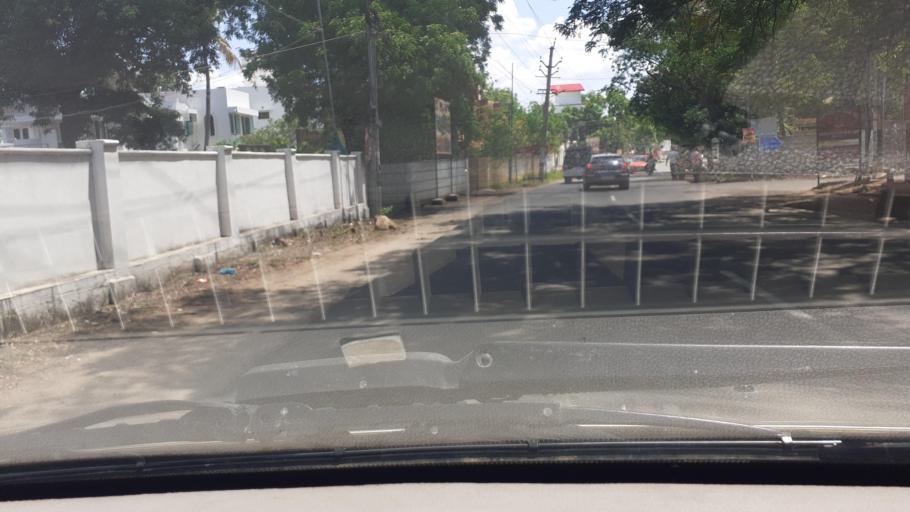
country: IN
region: Tamil Nadu
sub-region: Tirunelveli Kattabo
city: Tirunelveli
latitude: 8.7182
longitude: 77.7472
